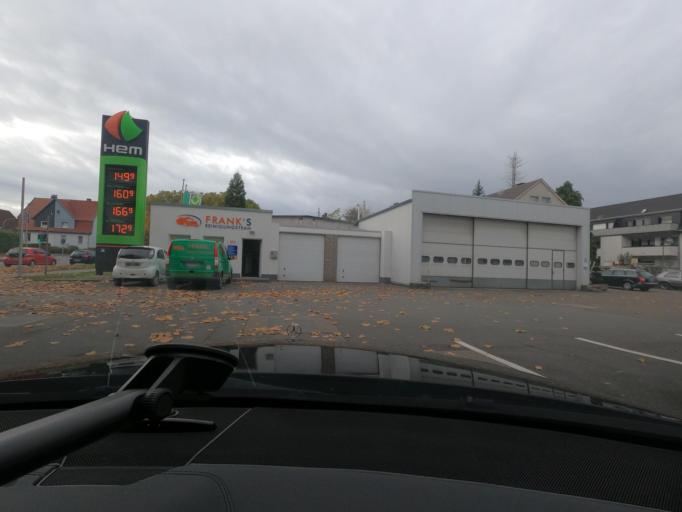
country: DE
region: North Rhine-Westphalia
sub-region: Regierungsbezirk Arnsberg
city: Soest
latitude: 51.5644
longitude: 8.0990
